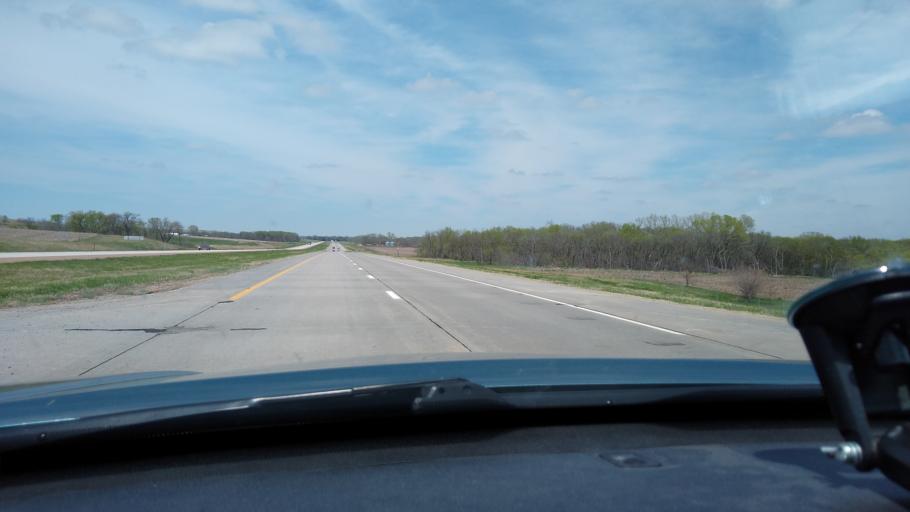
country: US
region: Kansas
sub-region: Republic County
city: Belleville
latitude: 39.7110
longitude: -97.6603
